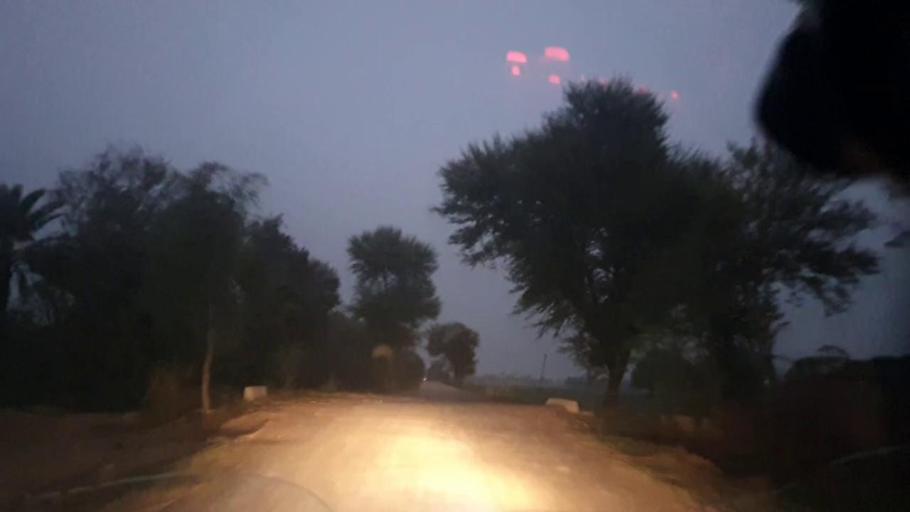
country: PK
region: Sindh
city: Hingorja
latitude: 27.2173
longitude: 68.3780
